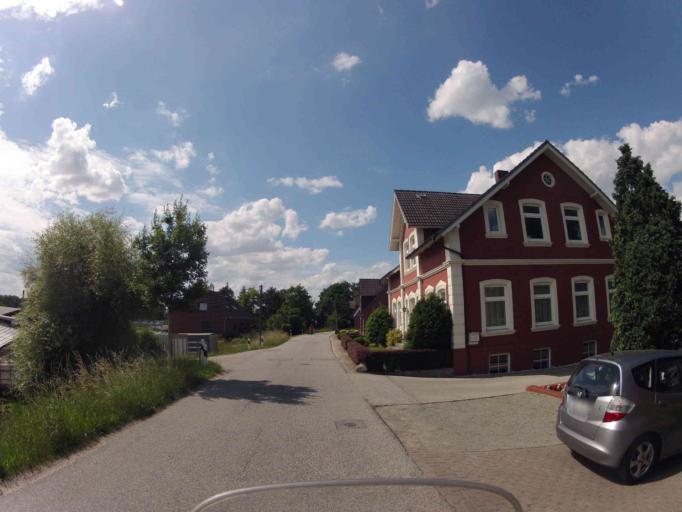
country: DE
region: Hamburg
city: Rothenburgsort
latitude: 53.4801
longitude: 10.0884
